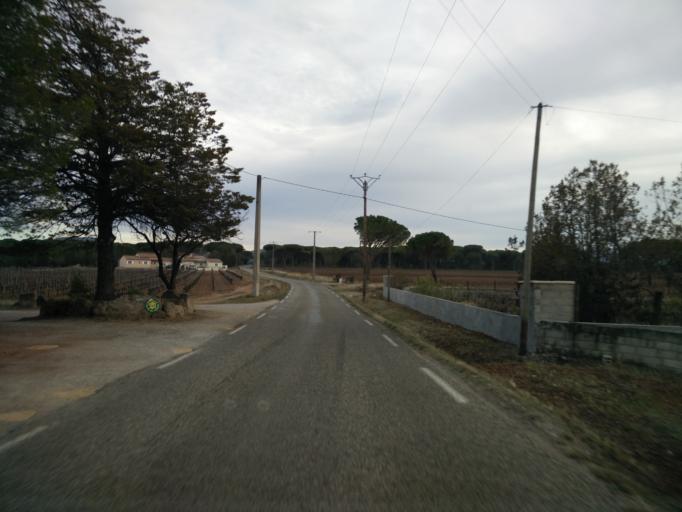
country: FR
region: Provence-Alpes-Cote d'Azur
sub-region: Departement du Var
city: Vidauban
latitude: 43.3967
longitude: 6.4340
